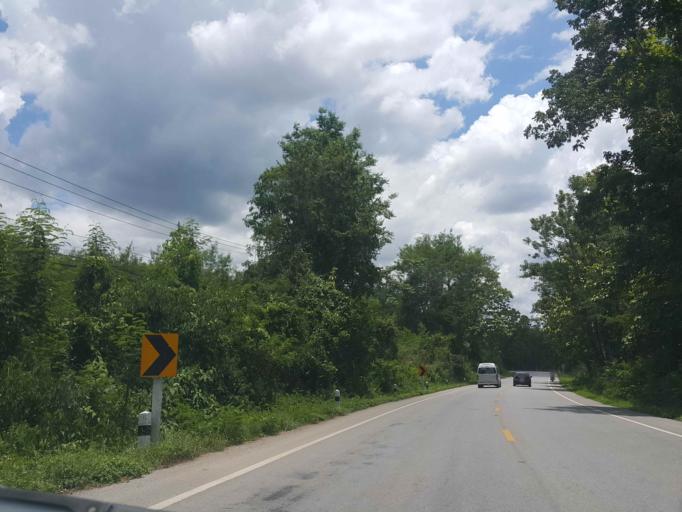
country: TH
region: Nan
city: Wiang Sa
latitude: 18.5205
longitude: 100.5836
